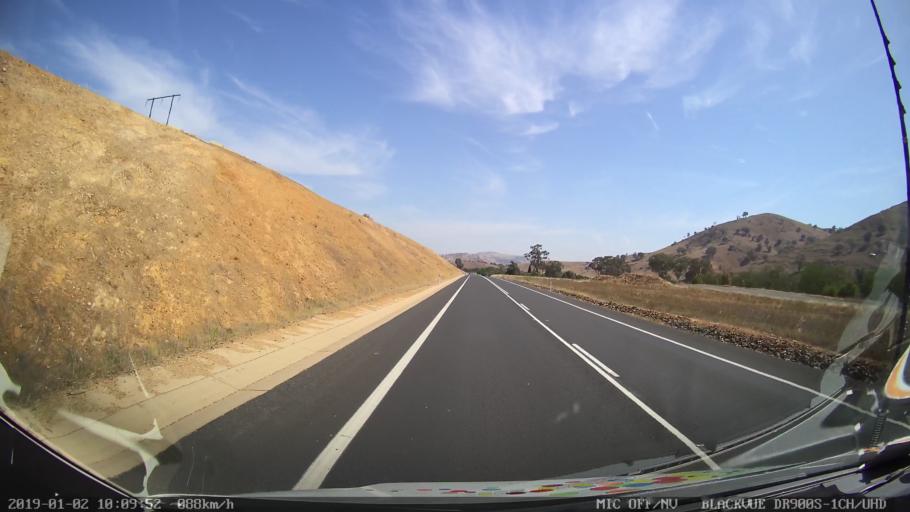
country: AU
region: New South Wales
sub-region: Gundagai
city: Gundagai
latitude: -35.1116
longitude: 148.0974
